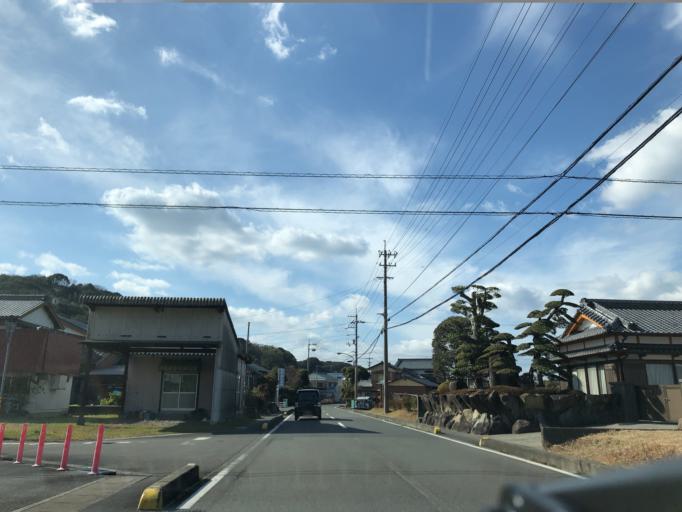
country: JP
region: Kochi
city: Sukumo
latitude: 32.9283
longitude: 132.6870
